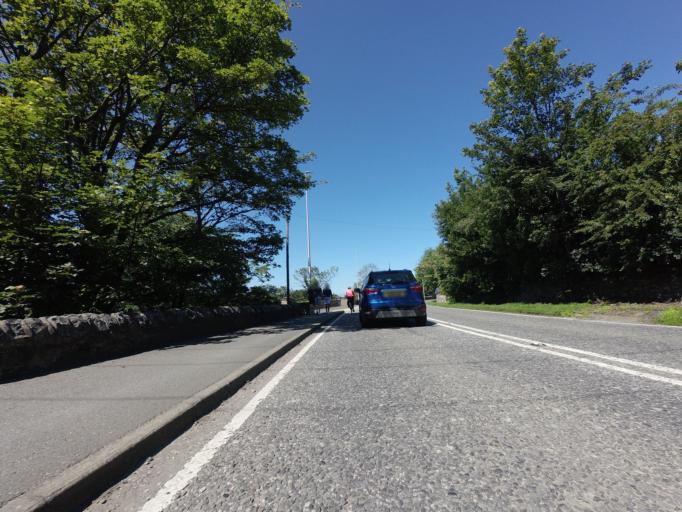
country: GB
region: Scotland
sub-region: Aberdeenshire
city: Macduff
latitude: 57.6595
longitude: -2.5115
